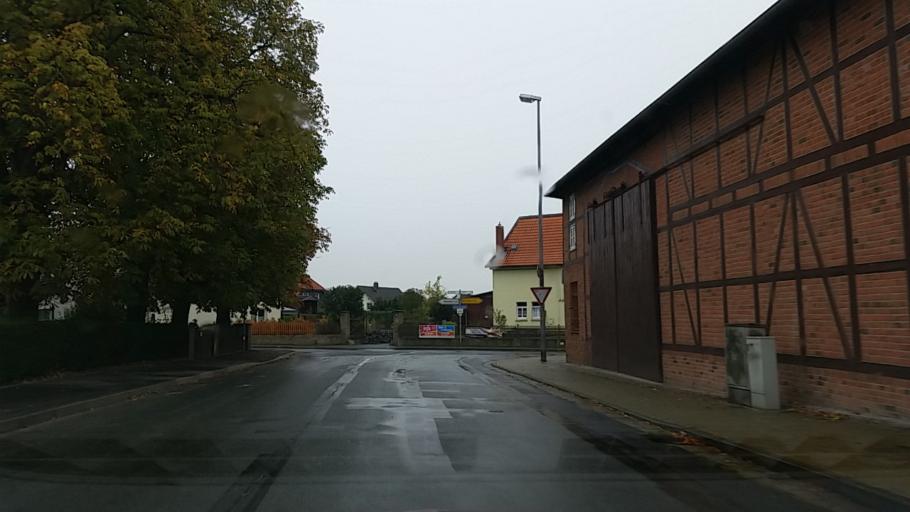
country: DE
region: Lower Saxony
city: Leiferde
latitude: 52.1629
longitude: 10.4862
